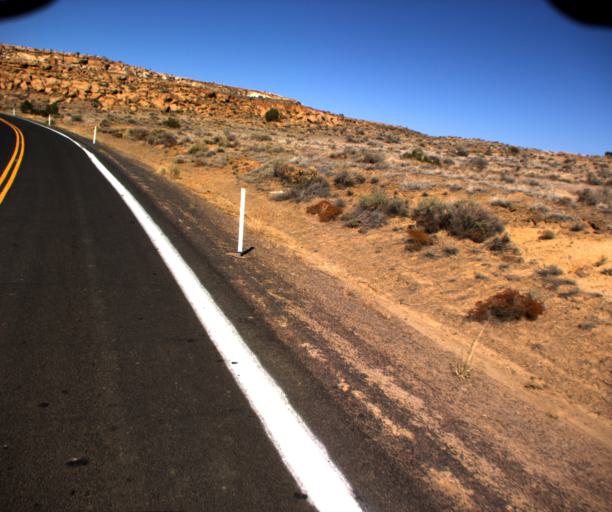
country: US
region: Arizona
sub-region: Navajo County
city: First Mesa
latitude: 35.8908
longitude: -110.6518
